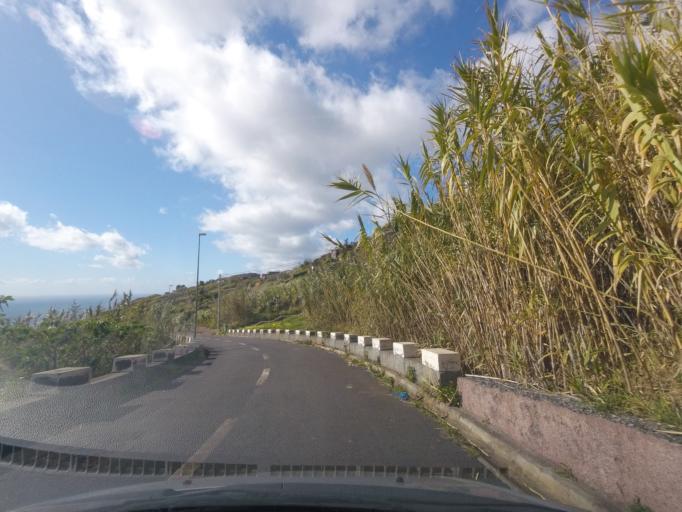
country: PT
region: Madeira
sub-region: Ribeira Brava
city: Campanario
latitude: 32.6628
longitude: -17.0225
